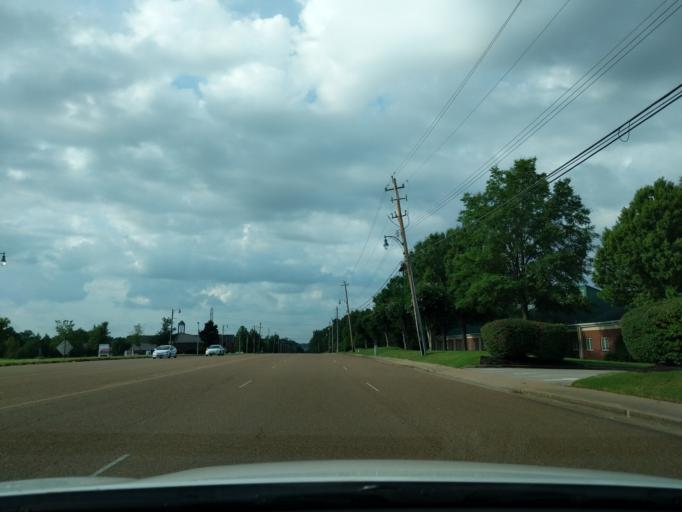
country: US
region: Tennessee
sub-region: Shelby County
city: Germantown
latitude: 35.0441
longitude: -89.7599
